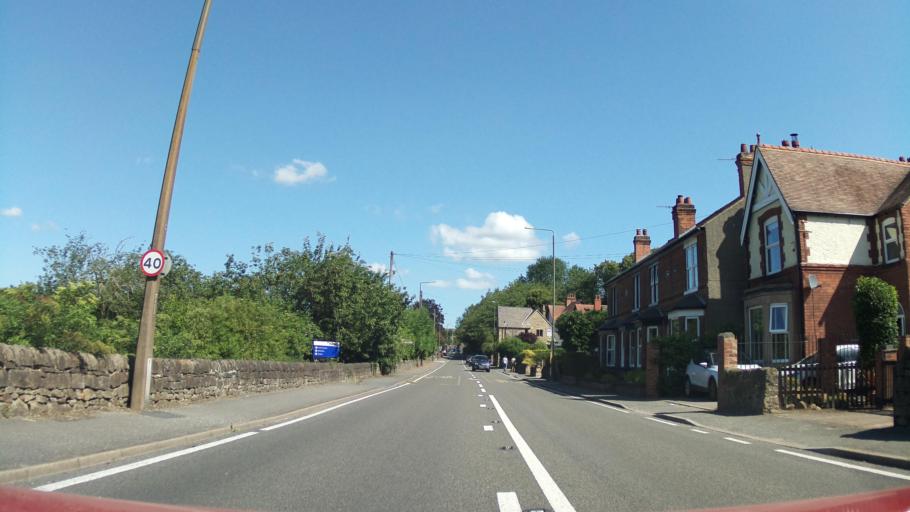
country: GB
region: England
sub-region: Derbyshire
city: Belper
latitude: 53.0093
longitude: -1.4809
